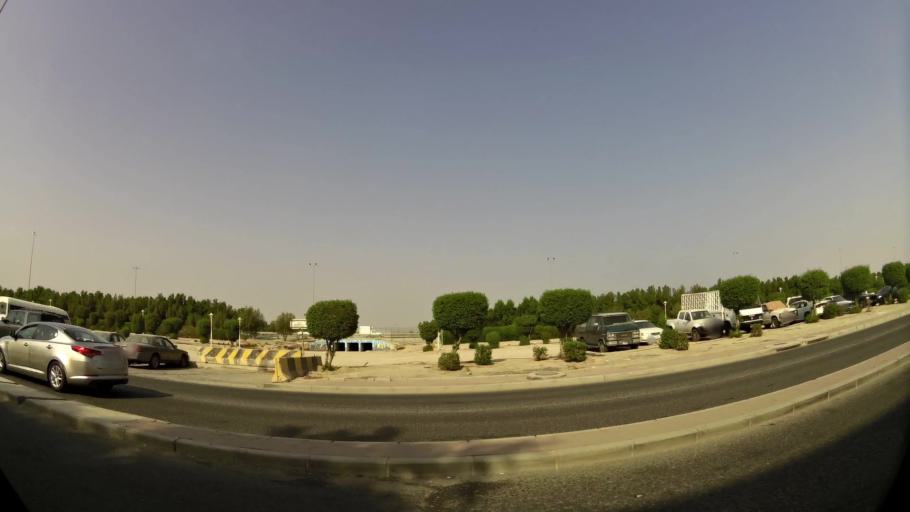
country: KW
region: Muhafazat al Jahra'
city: Al Jahra'
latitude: 29.3483
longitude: 47.6943
